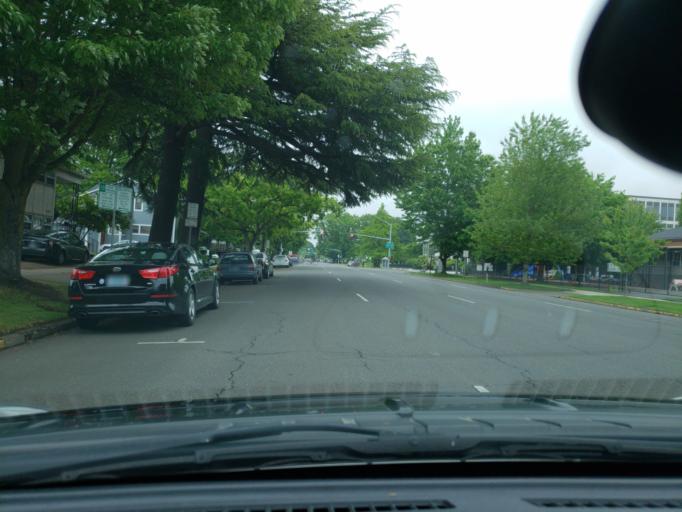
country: US
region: Oregon
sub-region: Marion County
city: Salem
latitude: 44.9420
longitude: -123.0317
